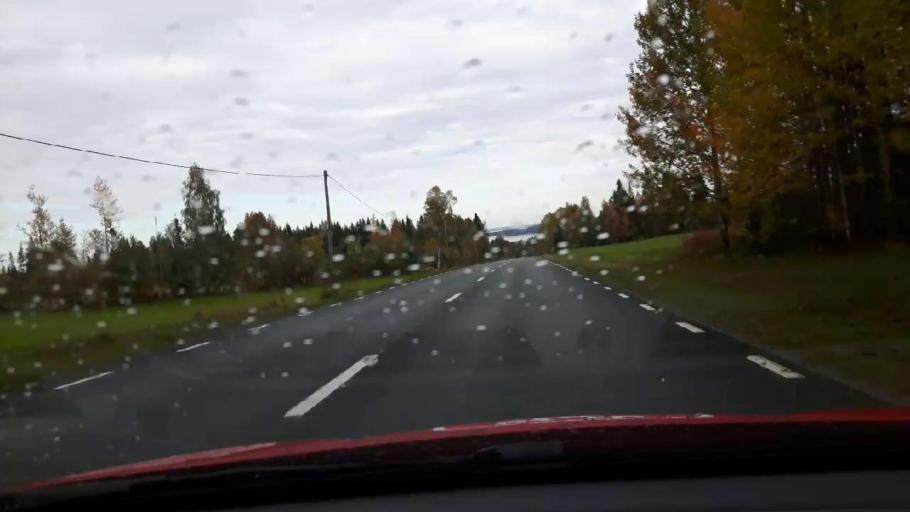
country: SE
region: Jaemtland
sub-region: Krokoms Kommun
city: Krokom
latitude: 63.1161
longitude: 14.2932
